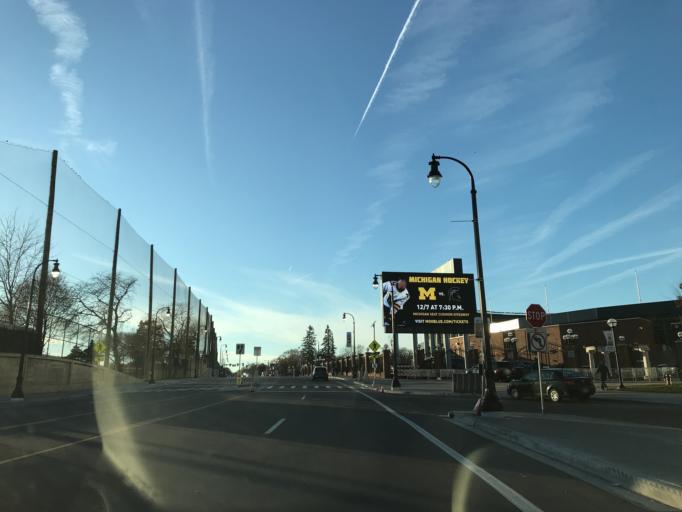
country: US
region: Michigan
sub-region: Washtenaw County
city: Ann Arbor
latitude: 42.2642
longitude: -83.7465
